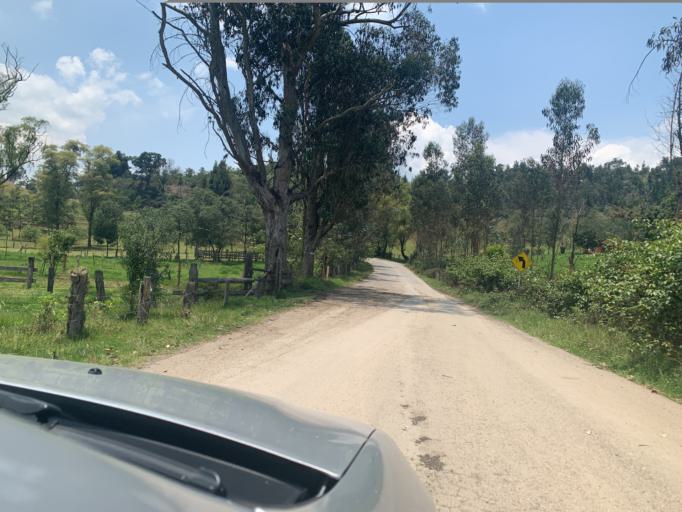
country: CO
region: Boyaca
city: Chiquinquira
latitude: 5.5756
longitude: -73.7464
